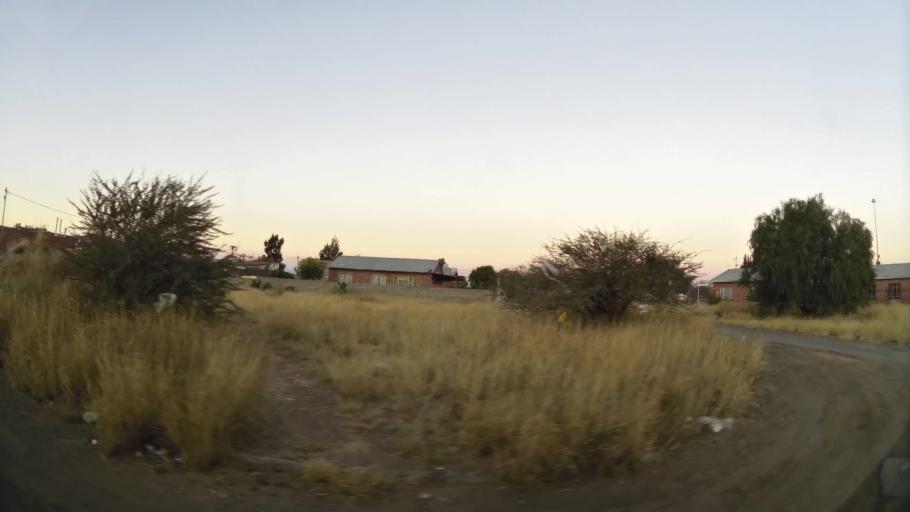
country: ZA
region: Northern Cape
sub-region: Frances Baard District Municipality
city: Kimberley
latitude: -28.7184
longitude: 24.7663
